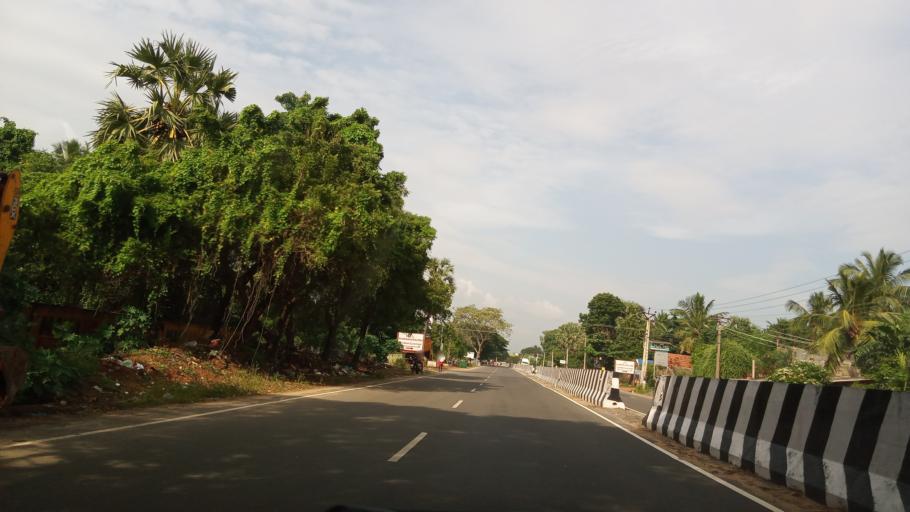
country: IN
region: Tamil Nadu
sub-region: Villupuram
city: Auroville
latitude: 12.0526
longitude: 79.8728
